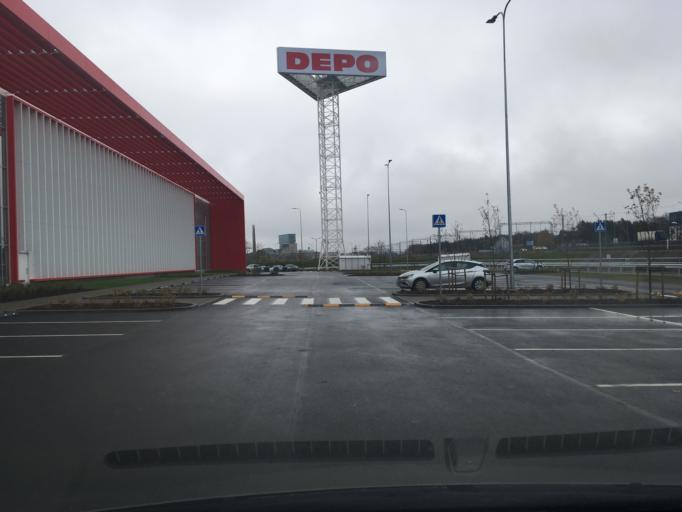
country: EE
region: Harju
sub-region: Tallinna linn
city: Tallinn
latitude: 59.4198
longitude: 24.7635
